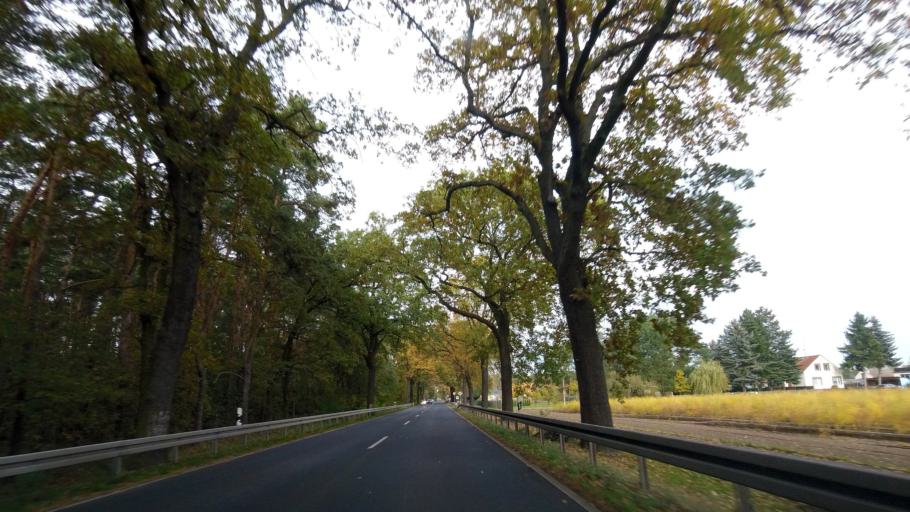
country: DE
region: Brandenburg
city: Beelitz
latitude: 52.1970
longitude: 12.9541
